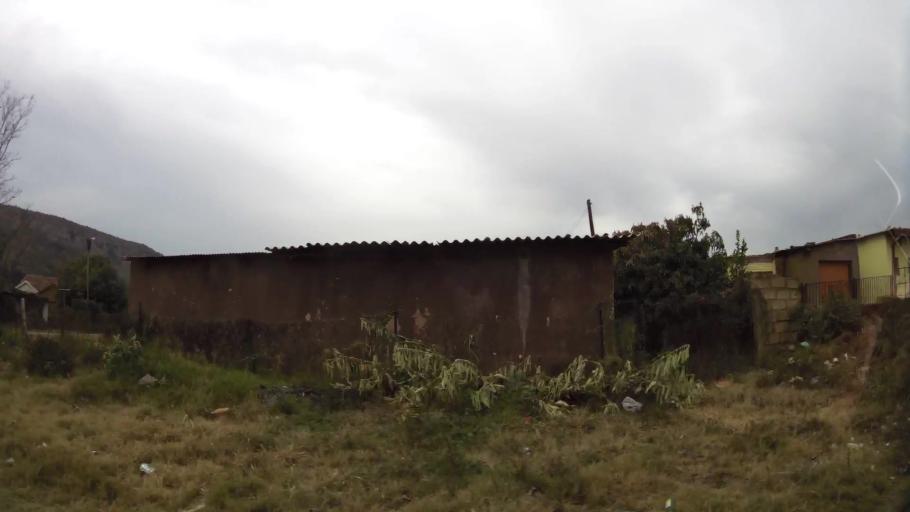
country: ZA
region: Gauteng
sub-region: City of Tshwane Metropolitan Municipality
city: Cullinan
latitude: -25.7059
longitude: 28.3602
